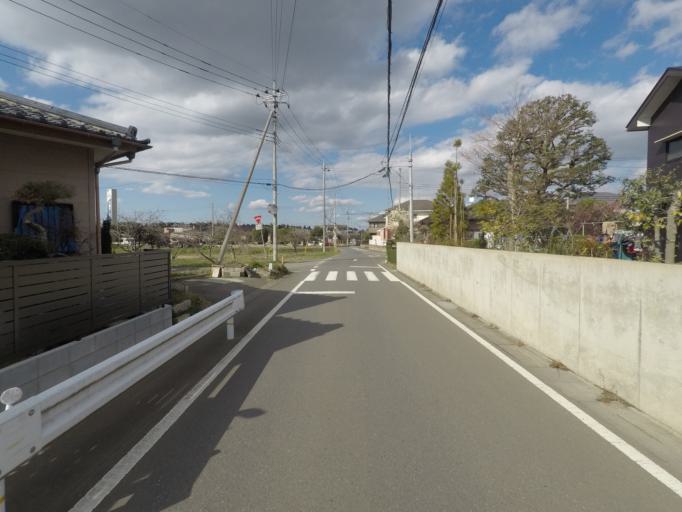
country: JP
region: Ibaraki
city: Naka
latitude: 36.0389
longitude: 140.1423
